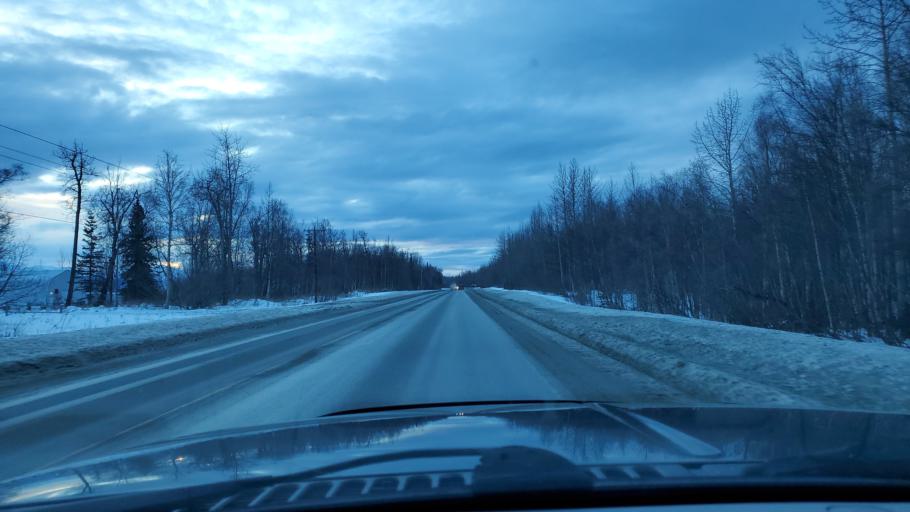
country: US
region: Alaska
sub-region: Matanuska-Susitna Borough
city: Farm Loop
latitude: 61.6732
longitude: -149.0666
